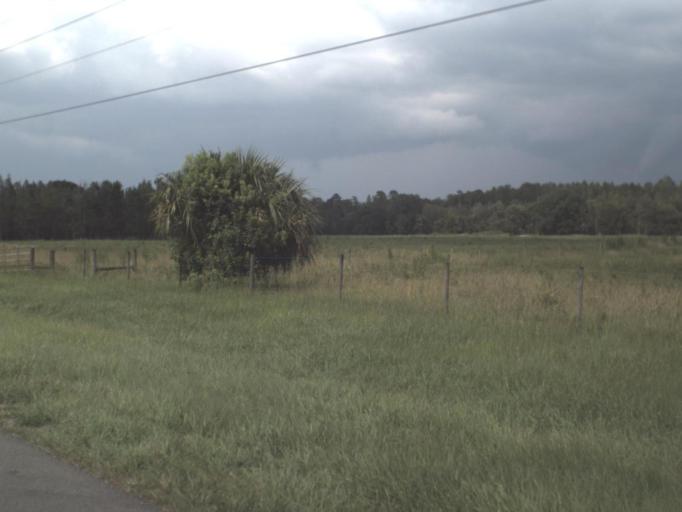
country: US
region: Florida
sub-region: Pasco County
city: Shady Hills
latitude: 28.3282
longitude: -82.5015
